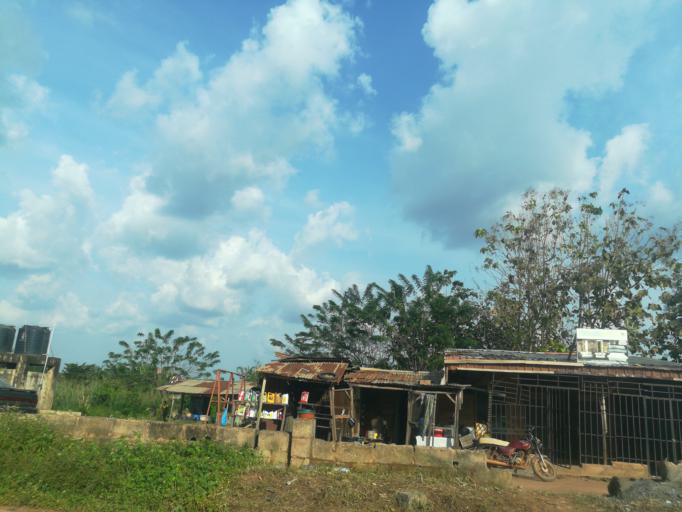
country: NG
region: Oyo
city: Ibadan
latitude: 7.3880
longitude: 3.8187
